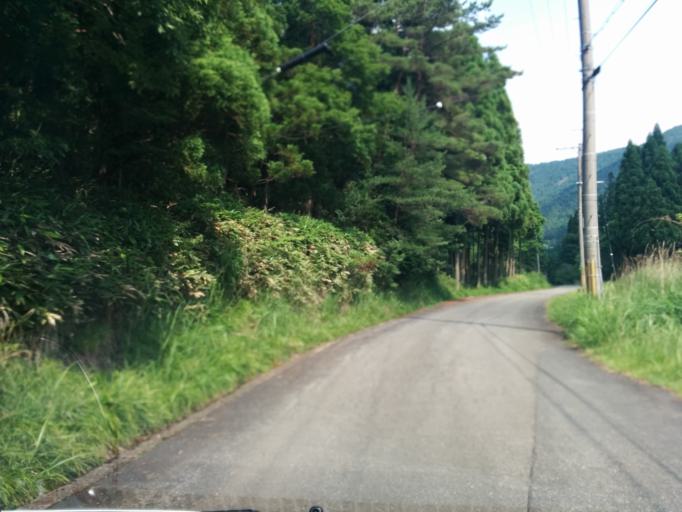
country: JP
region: Kyoto
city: Miyazu
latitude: 35.4588
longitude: 135.1230
